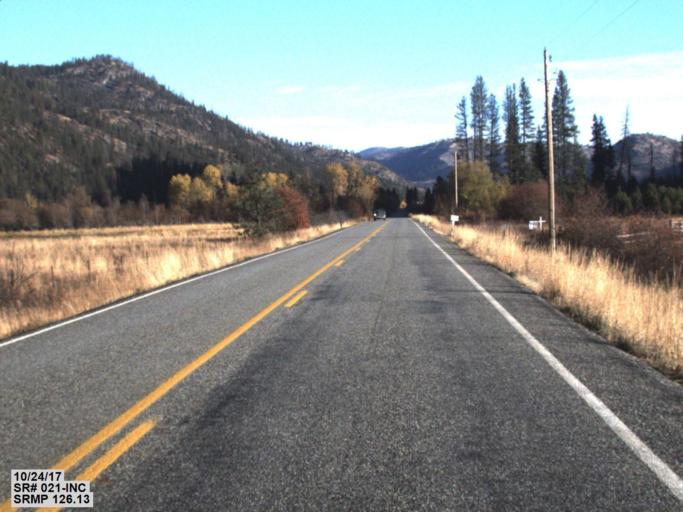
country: US
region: Washington
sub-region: Okanogan County
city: Coulee Dam
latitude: 48.2072
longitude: -118.7124
